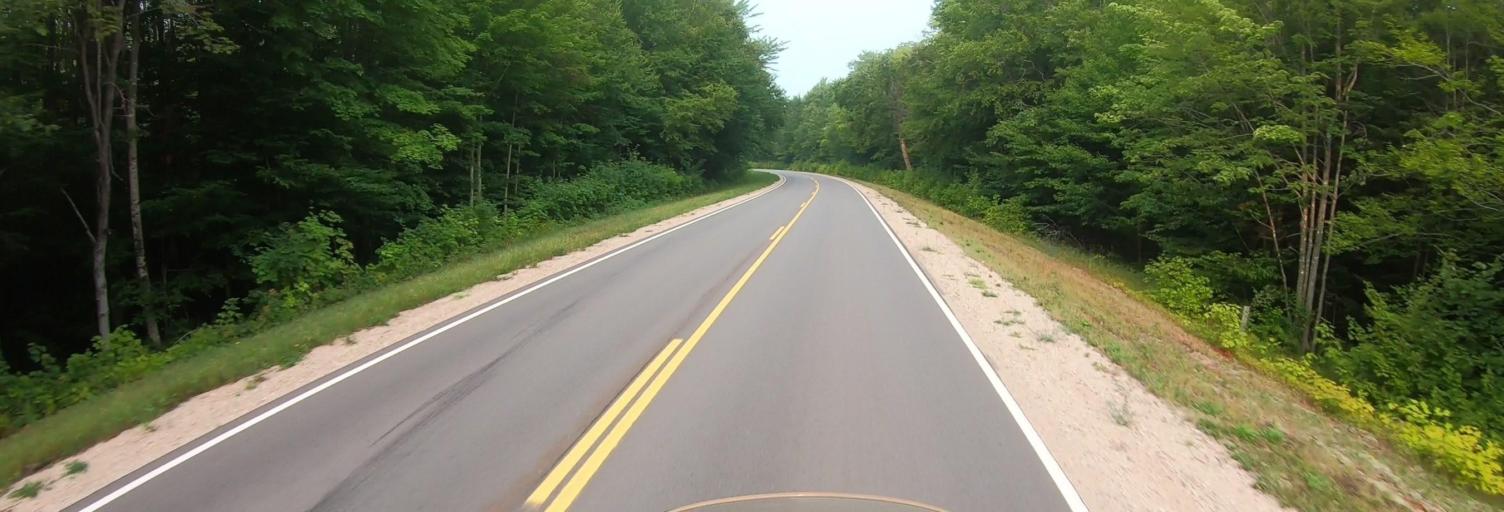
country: US
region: Michigan
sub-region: Luce County
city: Newberry
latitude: 46.4870
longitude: -85.0460
